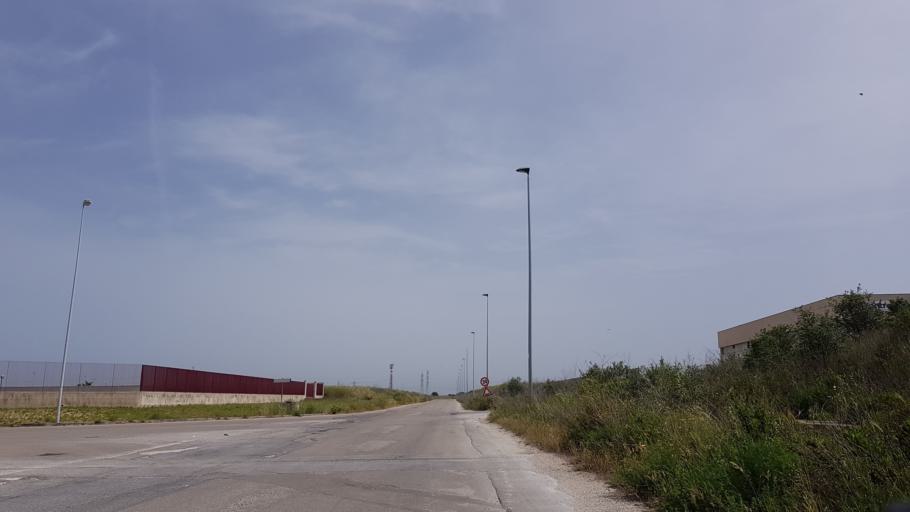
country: IT
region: Apulia
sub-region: Provincia di Brindisi
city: La Rosa
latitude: 40.6232
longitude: 17.9691
